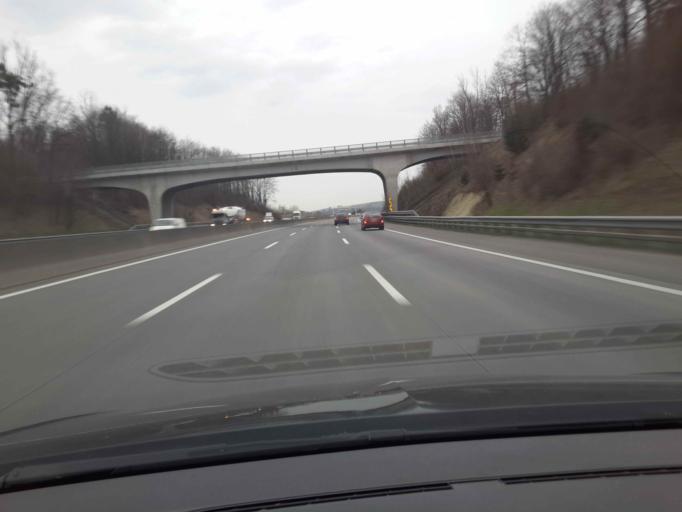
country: AT
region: Lower Austria
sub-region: Politischer Bezirk Melk
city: Blindenmarkt
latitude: 48.1296
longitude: 15.0046
